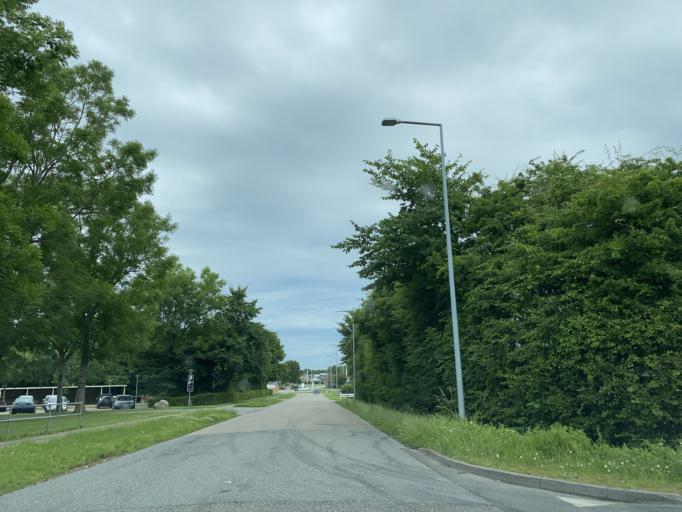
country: DK
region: South Denmark
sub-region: Sonderborg Kommune
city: Sonderborg
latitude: 54.9220
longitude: 9.7995
